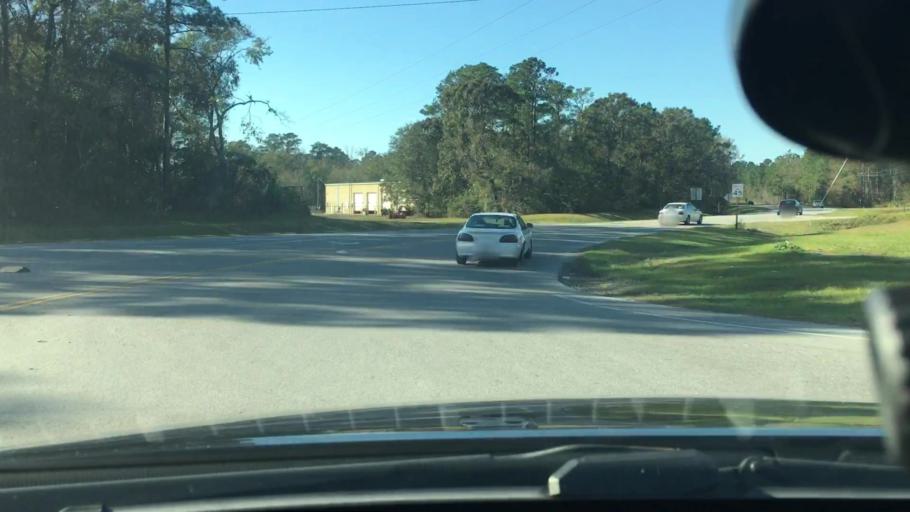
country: US
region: North Carolina
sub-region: Craven County
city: Vanceboro
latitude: 35.2167
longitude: -77.1207
